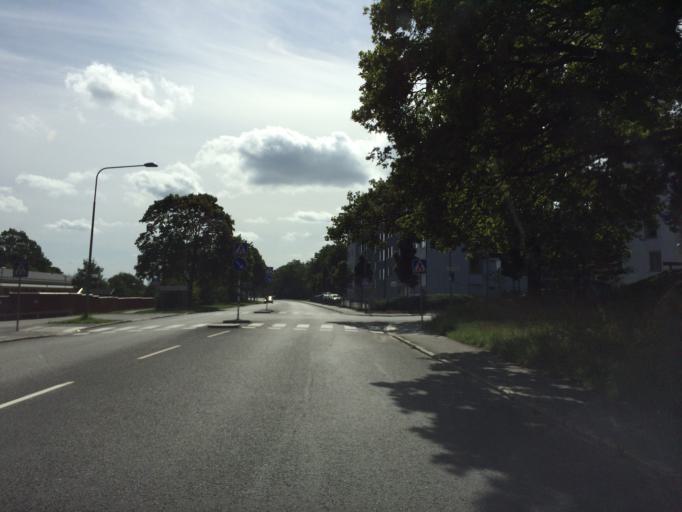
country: SE
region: Stockholm
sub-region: Huddinge Kommun
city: Segeltorp
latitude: 59.2927
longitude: 17.9785
